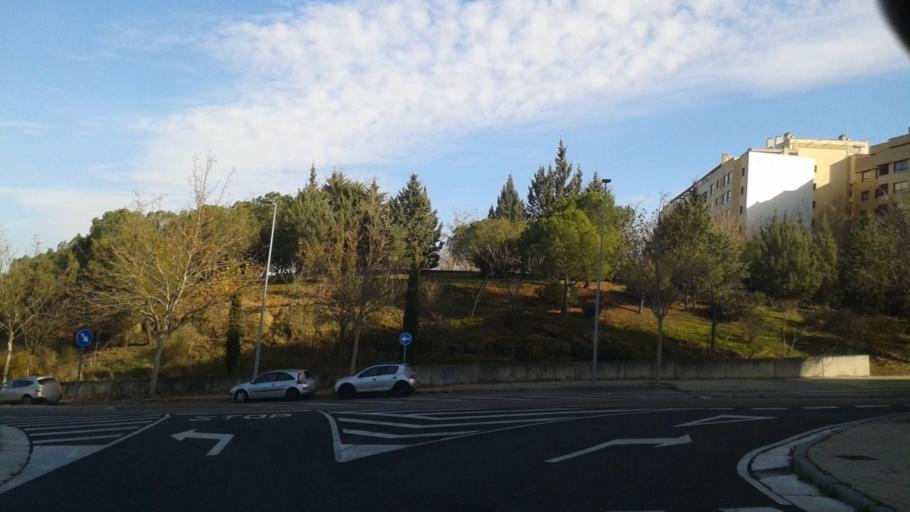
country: ES
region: Castille and Leon
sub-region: Provincia de Valladolid
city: Zaratan
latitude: 41.6374
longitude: -4.7685
